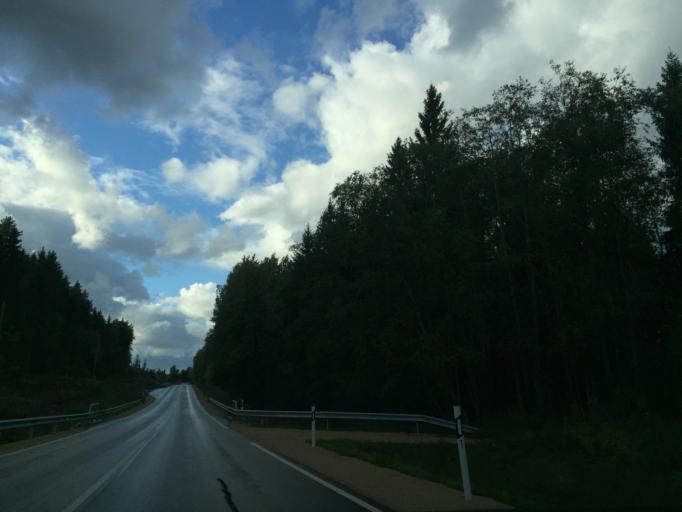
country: LV
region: Ligatne
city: Ligatne
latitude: 57.1588
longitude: 25.0608
